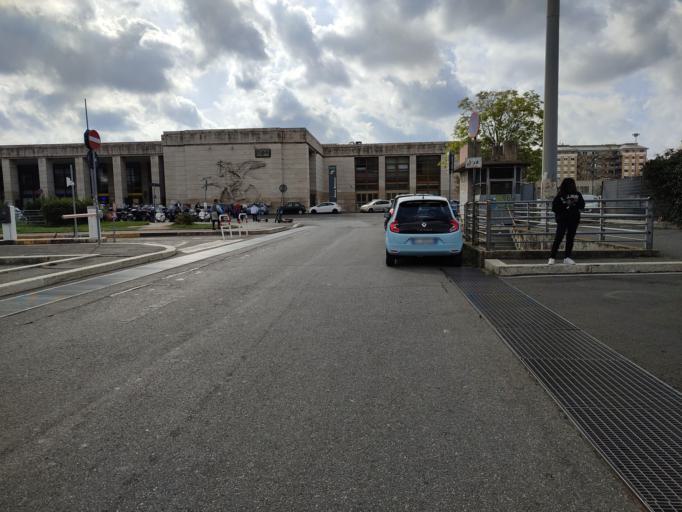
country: IT
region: Latium
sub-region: Citta metropolitana di Roma Capitale
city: Rome
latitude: 41.8738
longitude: 12.4837
